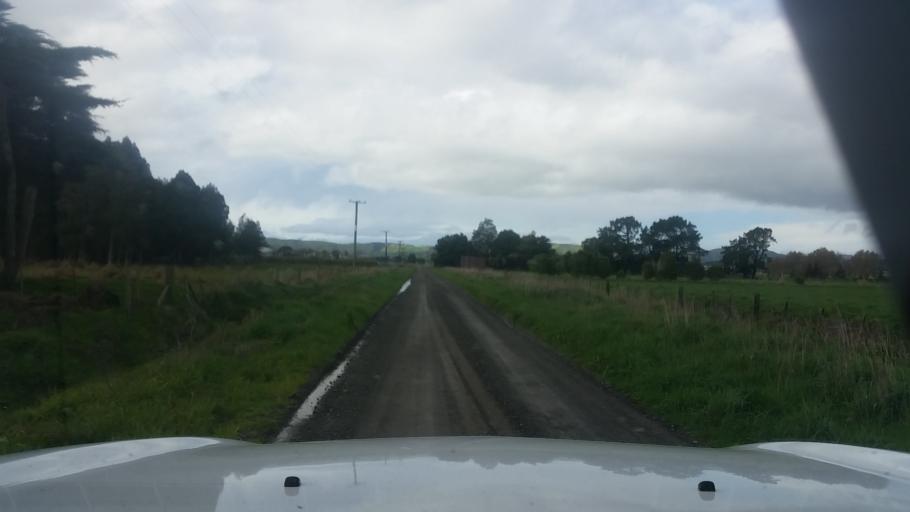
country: NZ
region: Wellington
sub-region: South Wairarapa District
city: Waipawa
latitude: -41.1431
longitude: 175.4106
